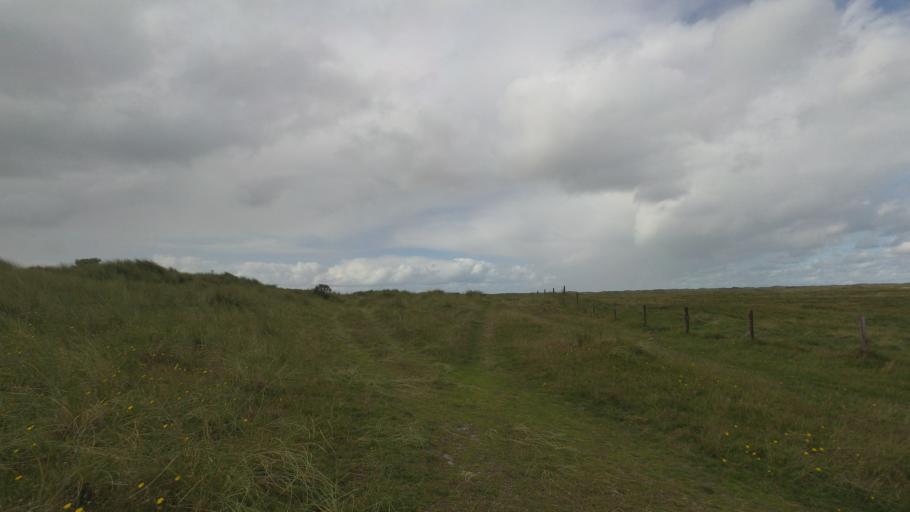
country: NL
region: Friesland
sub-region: Gemeente Ameland
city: Nes
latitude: 53.4520
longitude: 5.8498
